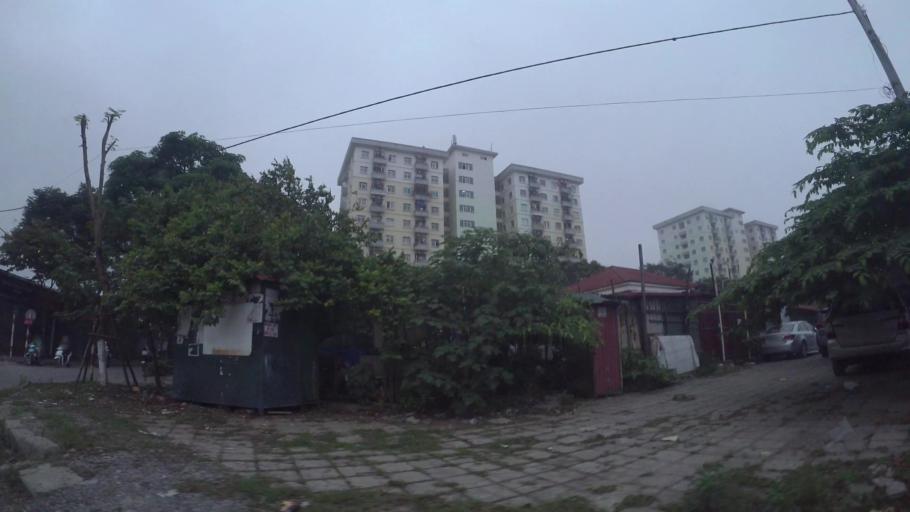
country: VN
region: Ha Noi
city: Thanh Xuan
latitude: 20.9867
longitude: 105.8269
